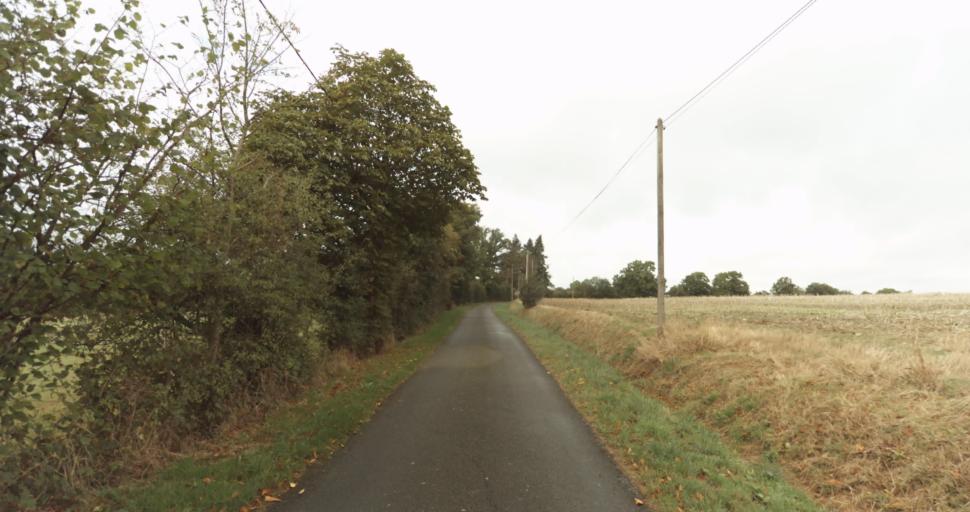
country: FR
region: Lower Normandy
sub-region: Departement de l'Orne
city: Sainte-Gauburge-Sainte-Colombe
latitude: 48.7338
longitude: 0.4813
